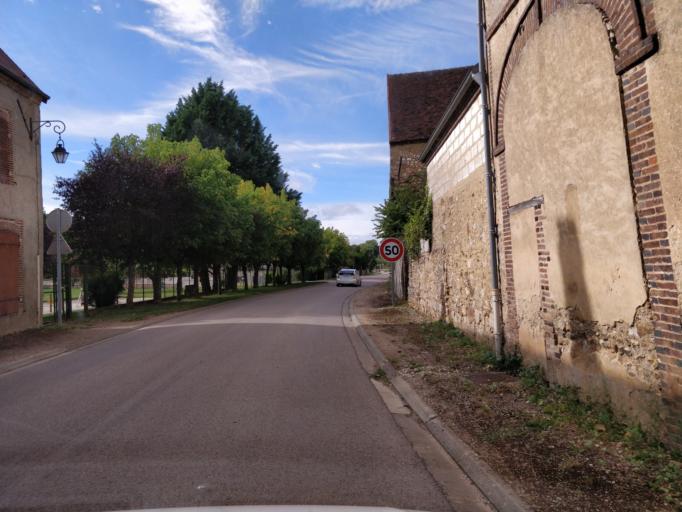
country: FR
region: Champagne-Ardenne
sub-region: Departement de l'Aube
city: Aix-en-Othe
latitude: 48.2091
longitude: 3.6292
